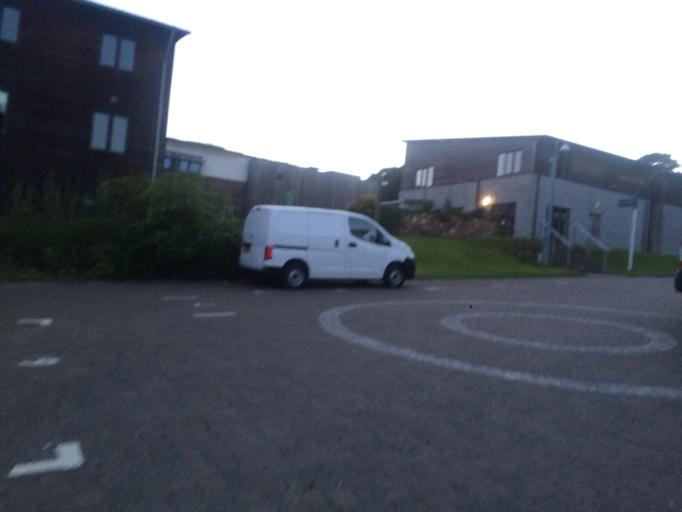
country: GB
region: England
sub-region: Cornwall
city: Penryn
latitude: 50.1711
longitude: -5.1211
